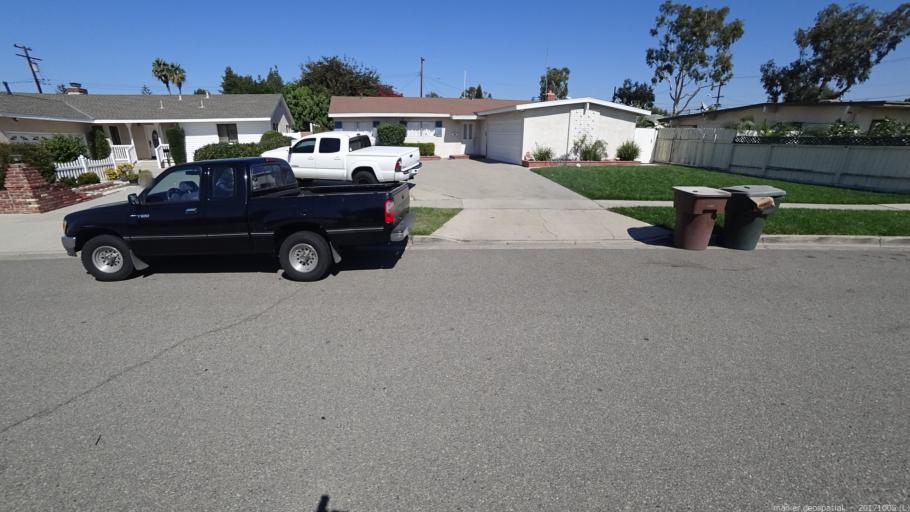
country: US
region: California
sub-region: Orange County
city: Stanton
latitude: 33.7917
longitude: -117.9681
